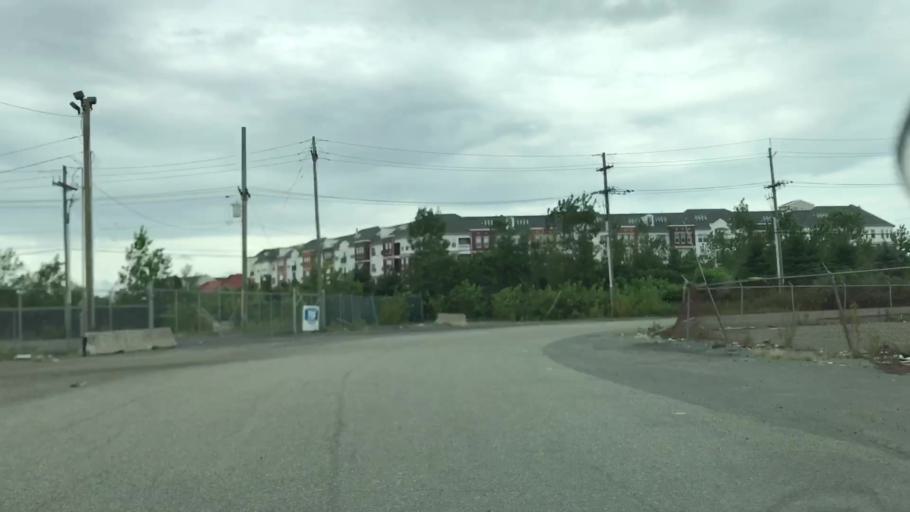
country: US
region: New Jersey
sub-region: Hudson County
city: Bayonne
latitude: 40.6733
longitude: -74.0963
